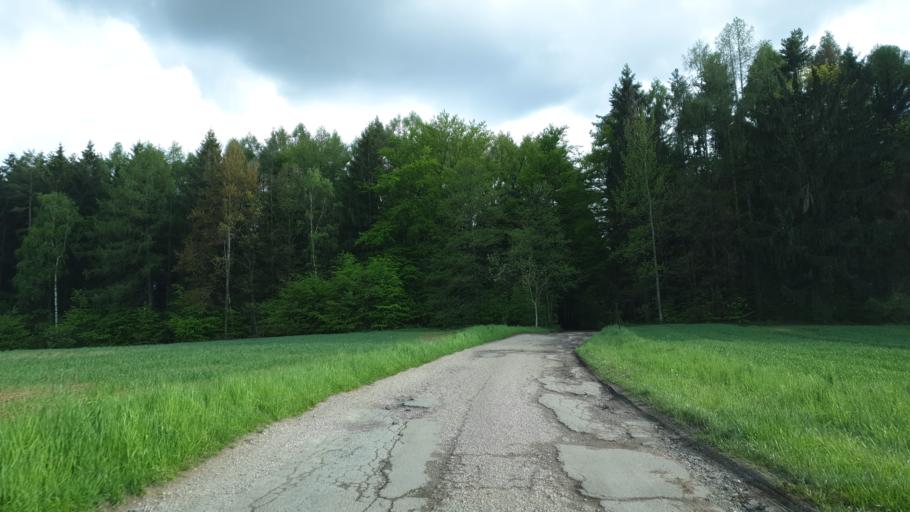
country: DE
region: Saxony
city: Hohndorf
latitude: 50.7235
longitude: 12.6667
